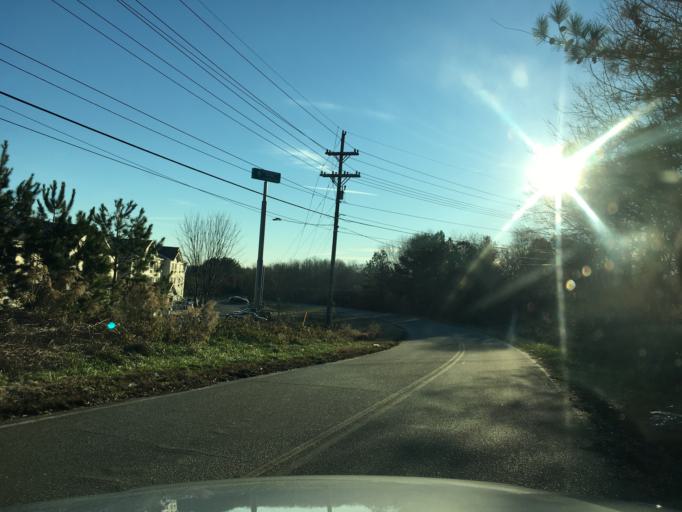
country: US
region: South Carolina
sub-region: Spartanburg County
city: Wellford
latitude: 34.9167
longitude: -82.1071
